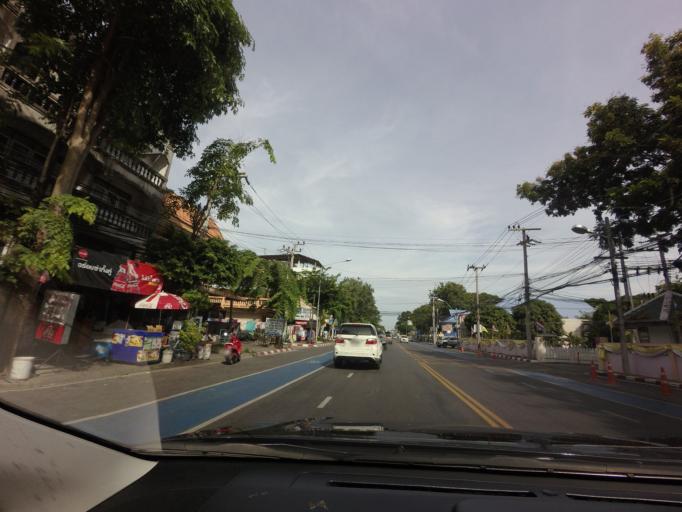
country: TH
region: Chon Buri
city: Chon Buri
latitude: 13.2897
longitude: 100.9139
